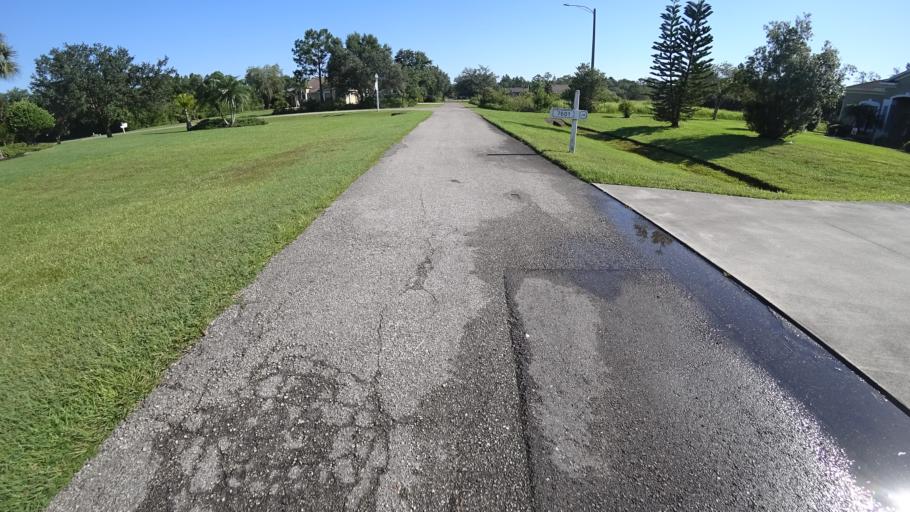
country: US
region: Florida
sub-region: Sarasota County
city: The Meadows
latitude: 27.4033
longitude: -82.3109
